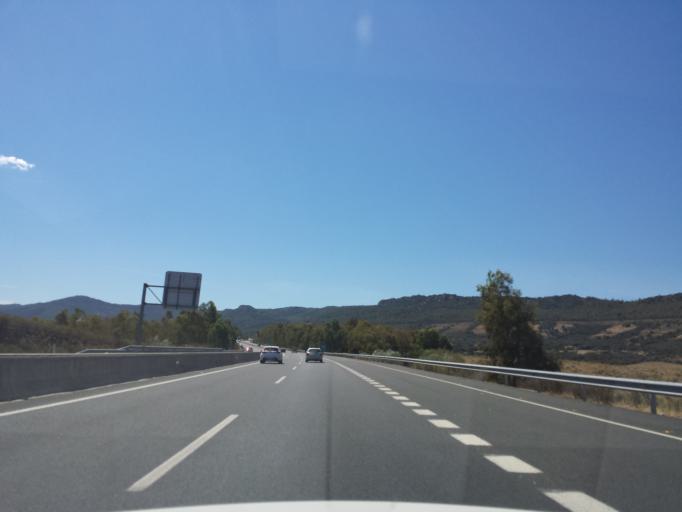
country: ES
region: Extremadura
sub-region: Provincia de Caceres
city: Romangordo
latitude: 39.7282
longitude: -5.7170
